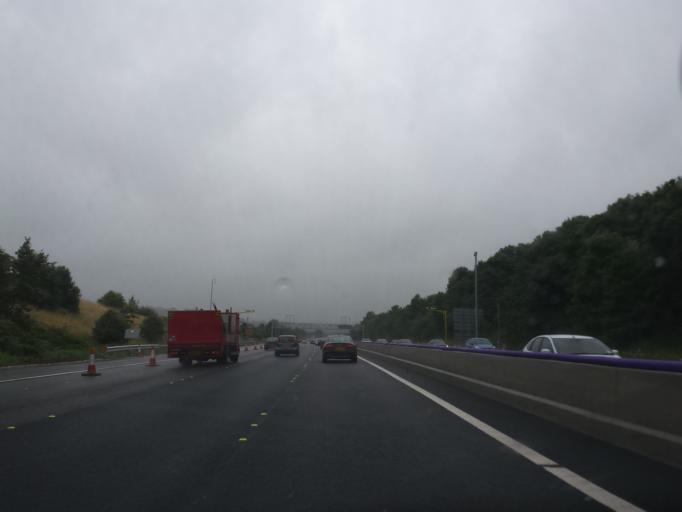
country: GB
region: England
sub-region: Derbyshire
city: Tibshelf
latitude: 53.1905
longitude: -1.3238
